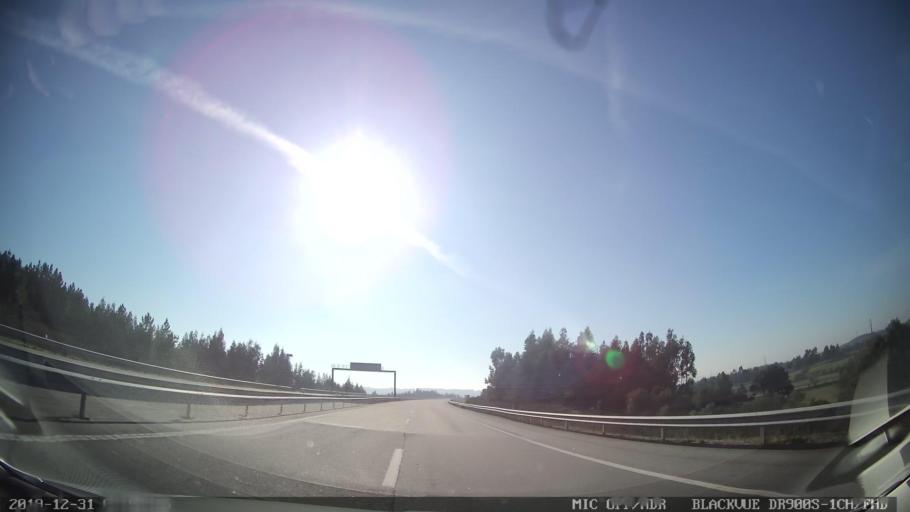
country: PT
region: Portalegre
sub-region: Nisa
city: Nisa
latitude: 39.6431
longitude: -7.7440
